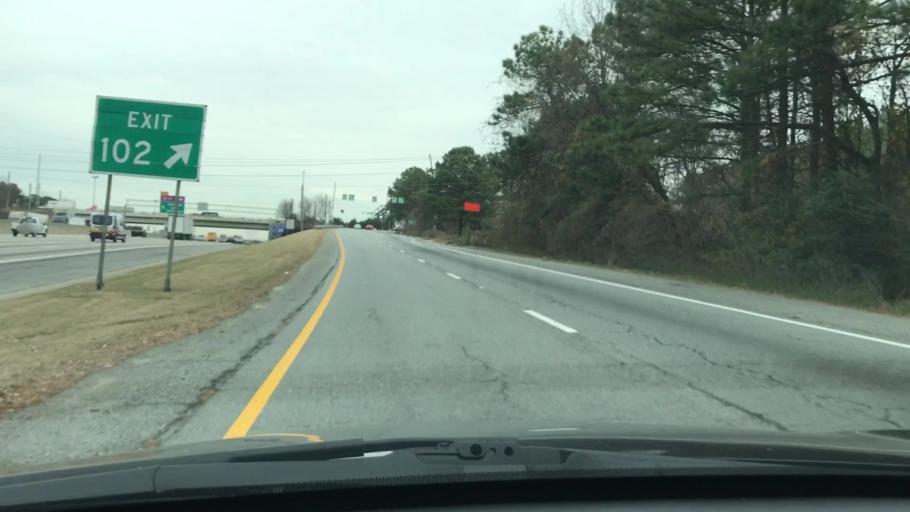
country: US
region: Georgia
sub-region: Gwinnett County
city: Lilburn
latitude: 33.9345
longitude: -84.1614
